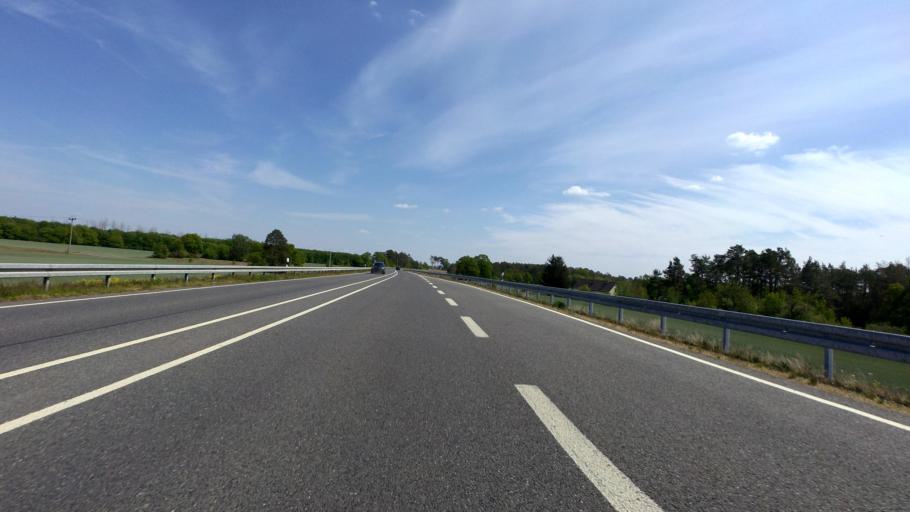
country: DE
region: Brandenburg
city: Cottbus
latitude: 51.7849
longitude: 14.3783
